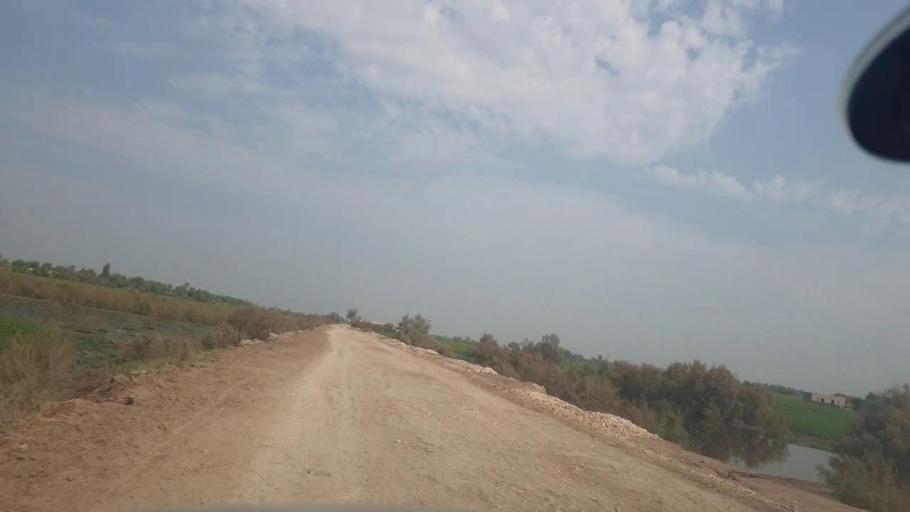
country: PK
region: Balochistan
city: Mehrabpur
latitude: 28.1022
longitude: 68.0924
